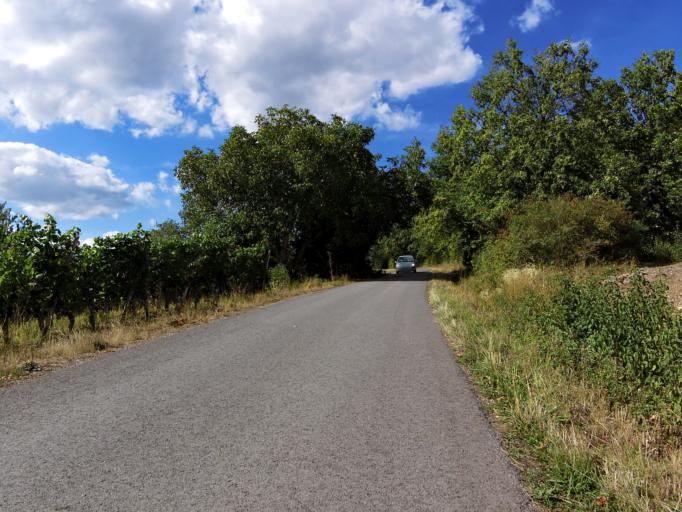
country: DE
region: Bavaria
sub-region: Regierungsbezirk Unterfranken
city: Veitshochheim
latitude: 49.8425
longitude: 9.8778
